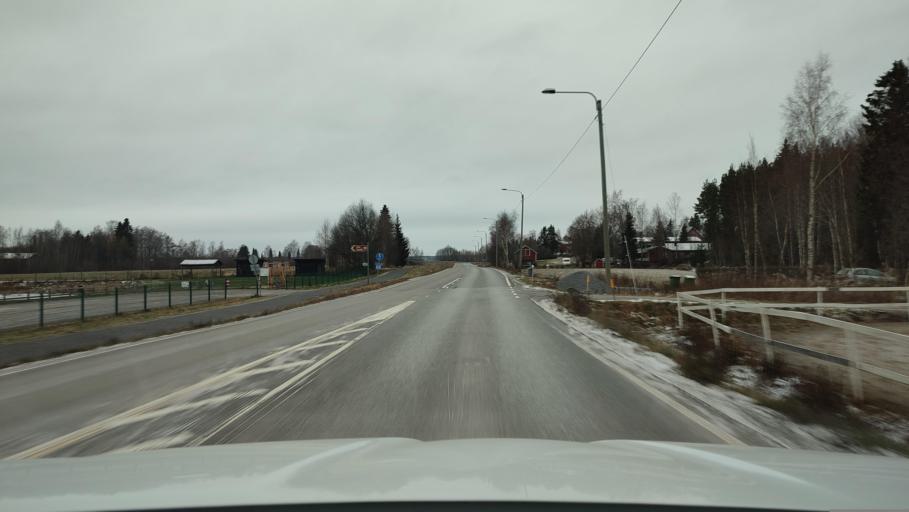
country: FI
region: Ostrobothnia
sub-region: Vaasa
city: Ristinummi
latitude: 63.0341
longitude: 21.7907
